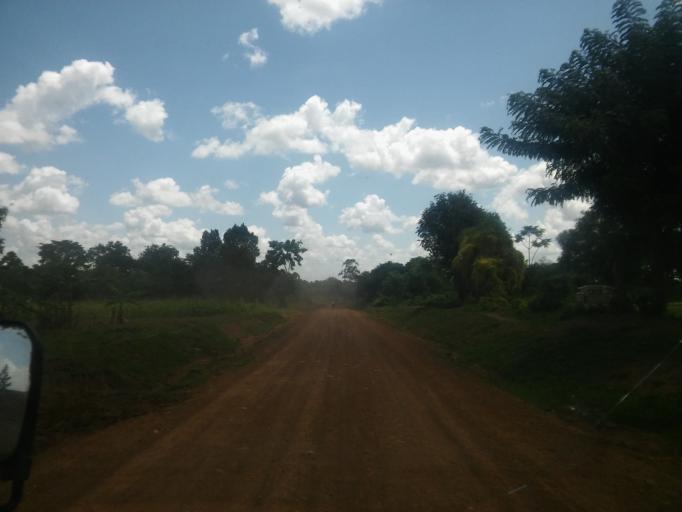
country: UG
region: Eastern Region
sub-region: Budaka District
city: Budaka
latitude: 1.1098
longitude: 33.9660
